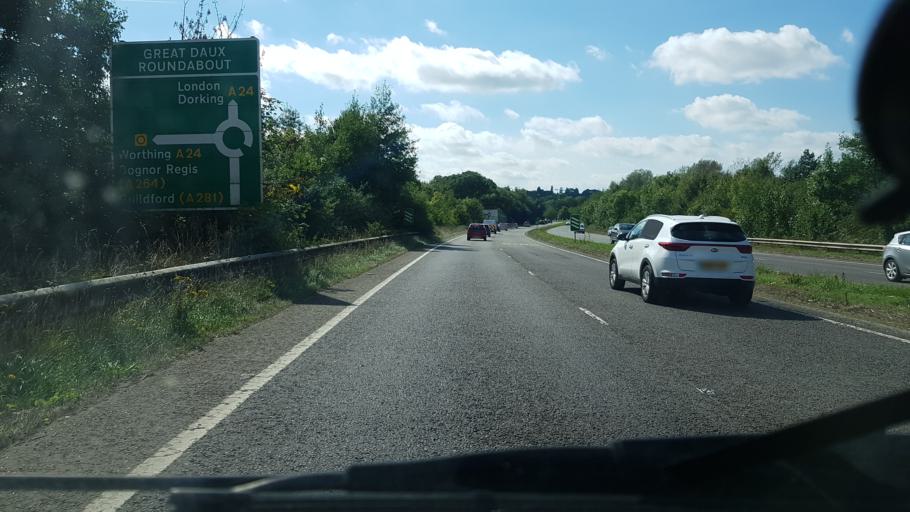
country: GB
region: England
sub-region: West Sussex
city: Horsham
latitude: 51.0878
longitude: -0.3277
